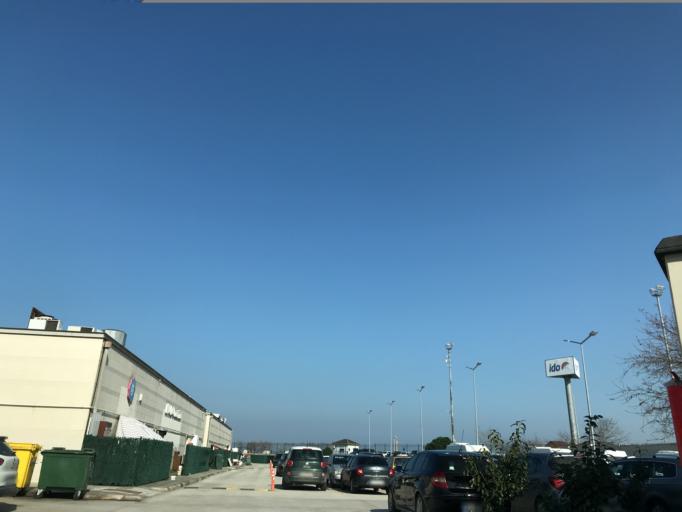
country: TR
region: Yalova
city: Yalova
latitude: 40.6600
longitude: 29.2775
